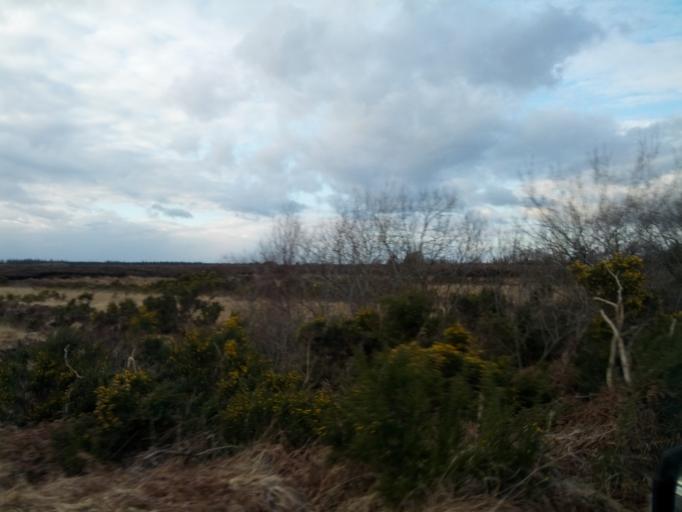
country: IE
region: Connaught
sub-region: County Galway
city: Athenry
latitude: 53.3630
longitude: -8.6661
